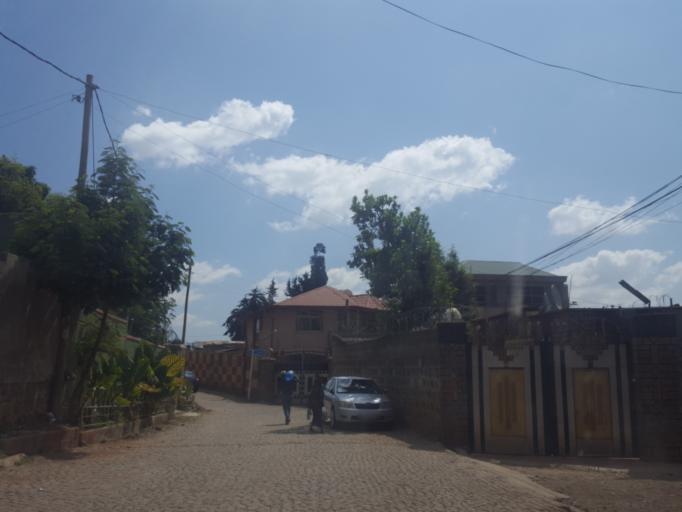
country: ET
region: Adis Abeba
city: Addis Ababa
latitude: 9.0560
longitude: 38.7258
